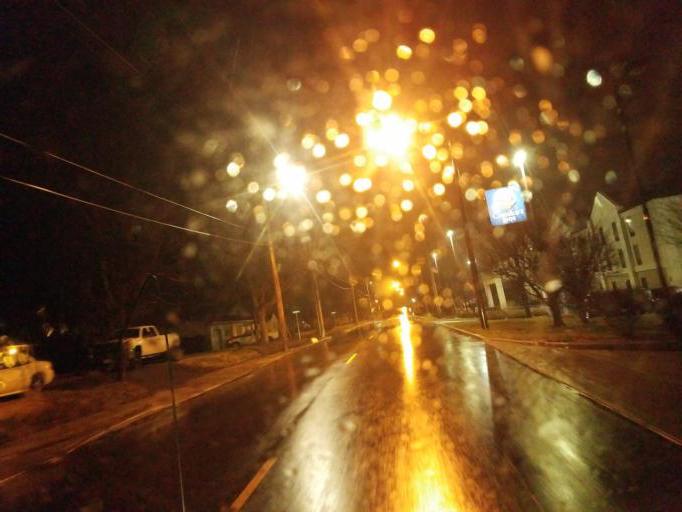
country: US
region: Missouri
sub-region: Franklin County
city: Pacific
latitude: 38.4861
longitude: -90.7570
